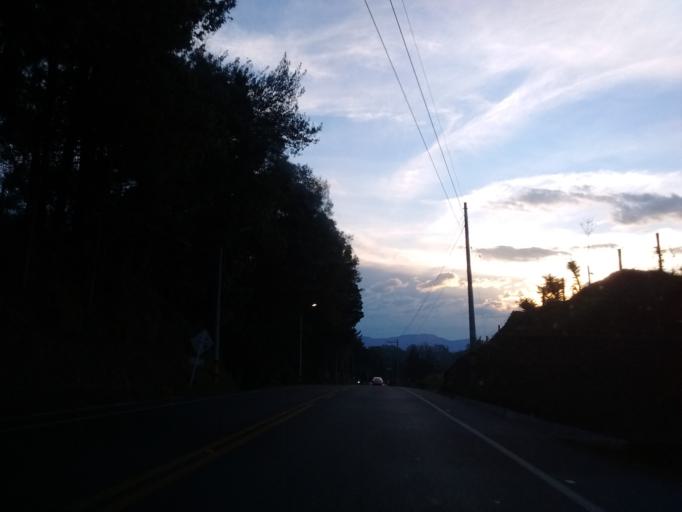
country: CO
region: Antioquia
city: Envigado
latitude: 6.1598
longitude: -75.5258
